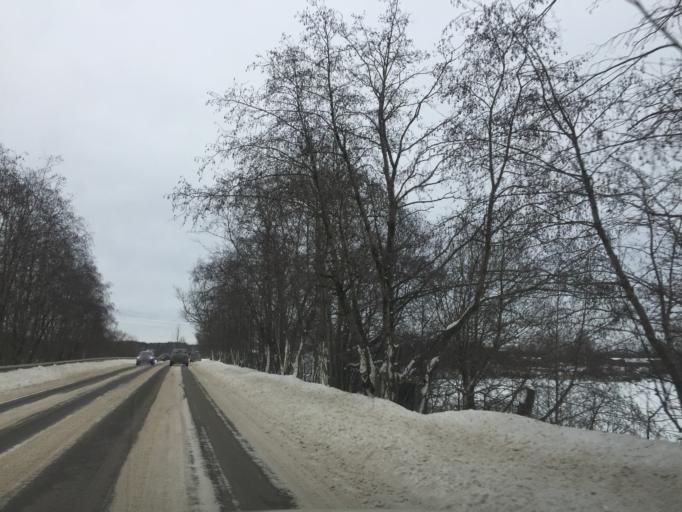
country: RU
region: Leningrad
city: Imeni Sverdlova
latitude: 59.7901
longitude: 30.7030
